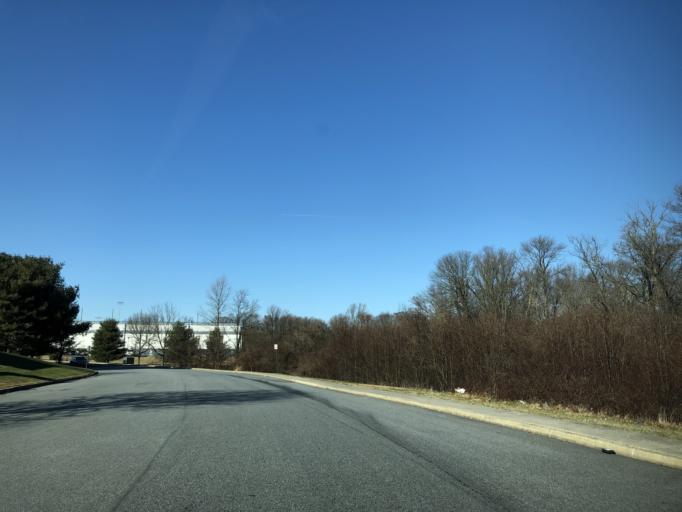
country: US
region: Pennsylvania
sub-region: Delaware County
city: Boothwyn
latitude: 39.8523
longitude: -75.4477
